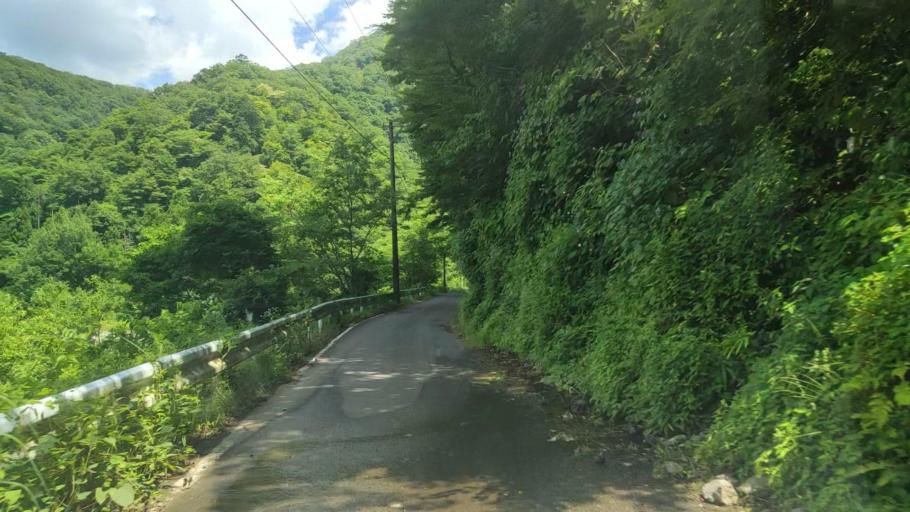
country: JP
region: Fukui
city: Ono
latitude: 35.7451
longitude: 136.5822
